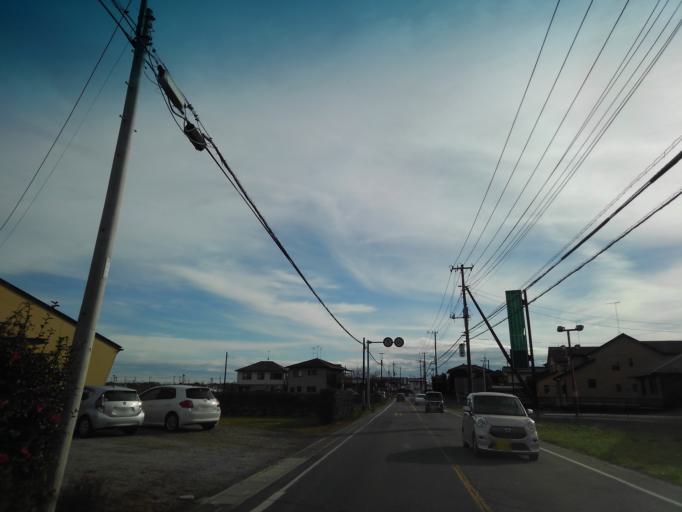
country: JP
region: Saitama
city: Morohongo
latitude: 35.9073
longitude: 139.3336
